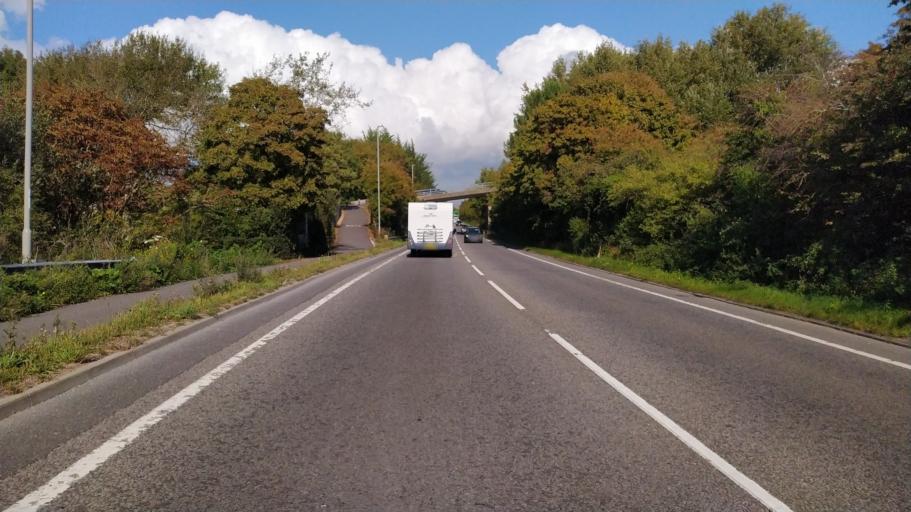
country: GB
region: England
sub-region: Dorset
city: Weymouth
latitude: 50.6292
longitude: -2.4720
